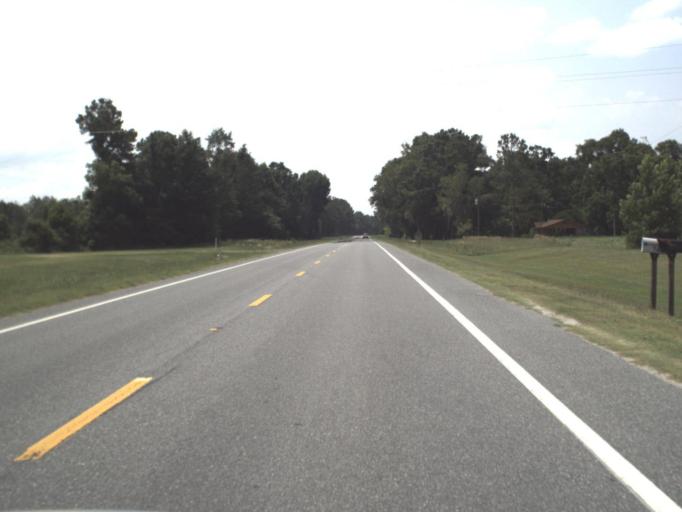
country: US
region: Florida
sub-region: Hamilton County
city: Jasper
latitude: 30.5412
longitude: -83.0518
